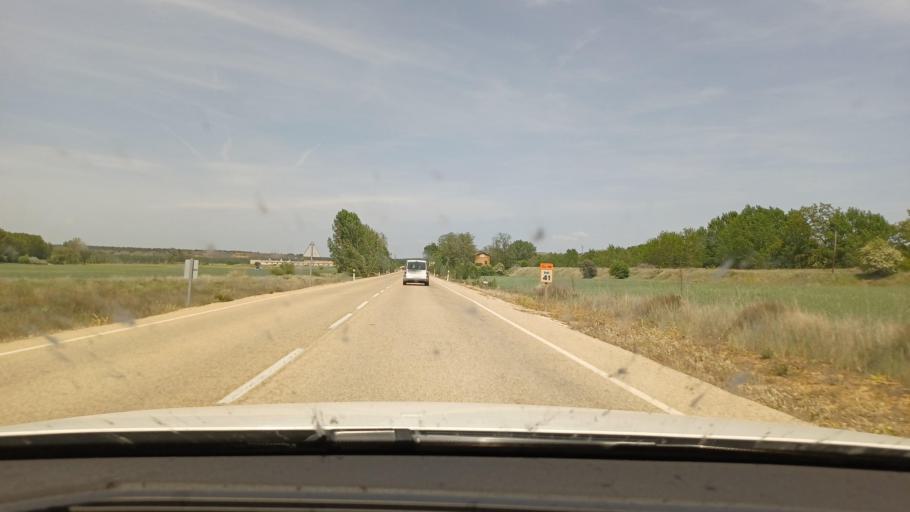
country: ES
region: Castille and Leon
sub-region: Provincia de Soria
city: Barca
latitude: 41.4666
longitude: -2.6089
